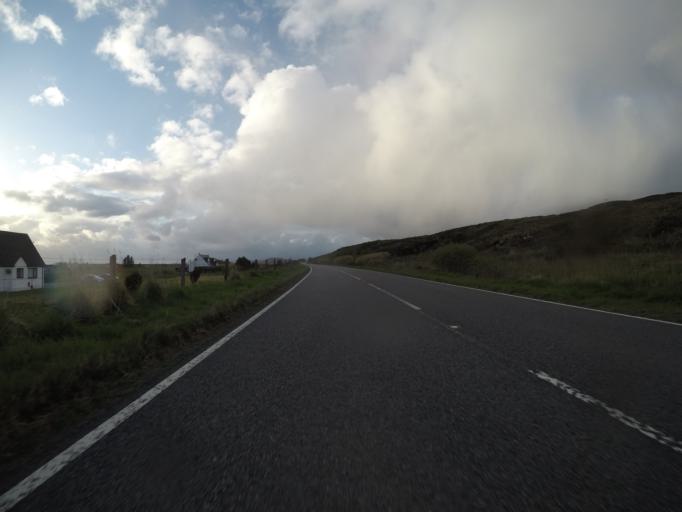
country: GB
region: Scotland
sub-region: Highland
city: Portree
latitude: 57.5601
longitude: -6.3635
